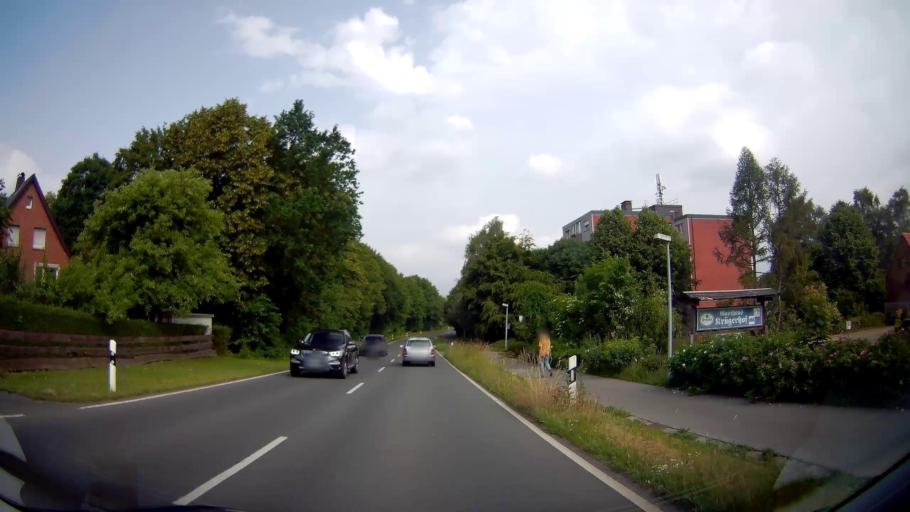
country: DE
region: North Rhine-Westphalia
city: Loehne
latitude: 52.1819
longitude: 8.7197
